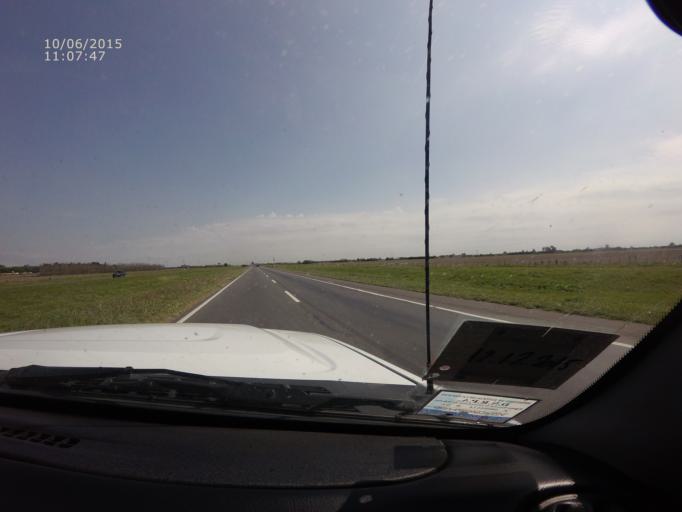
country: AR
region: Santa Fe
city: Arroyo Seco
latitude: -33.1846
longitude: -60.5114
